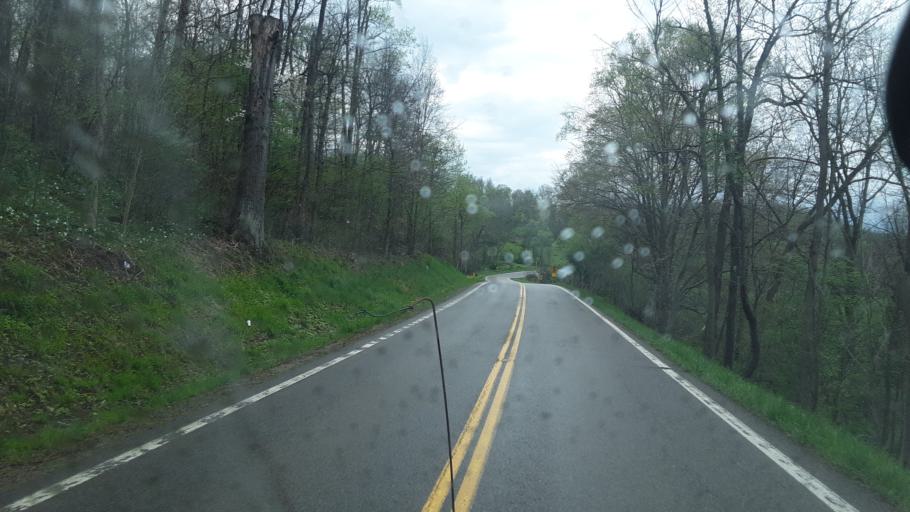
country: US
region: Ohio
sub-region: Guernsey County
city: Mantua
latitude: 40.0741
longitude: -81.7574
